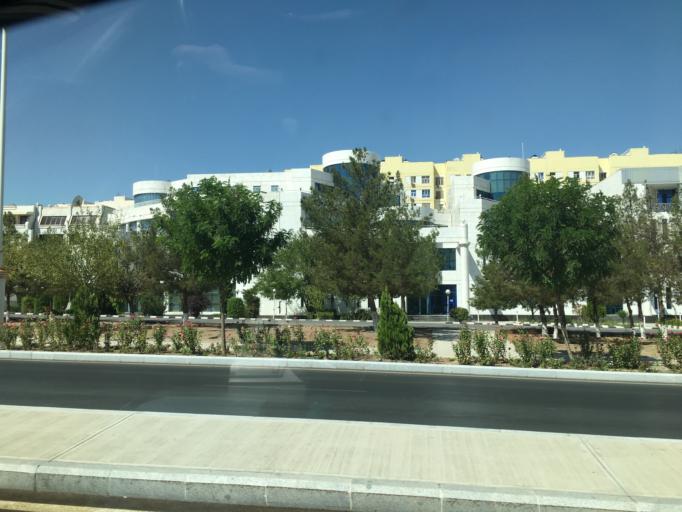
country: TM
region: Ahal
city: Ashgabat
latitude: 37.9048
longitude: 58.3889
